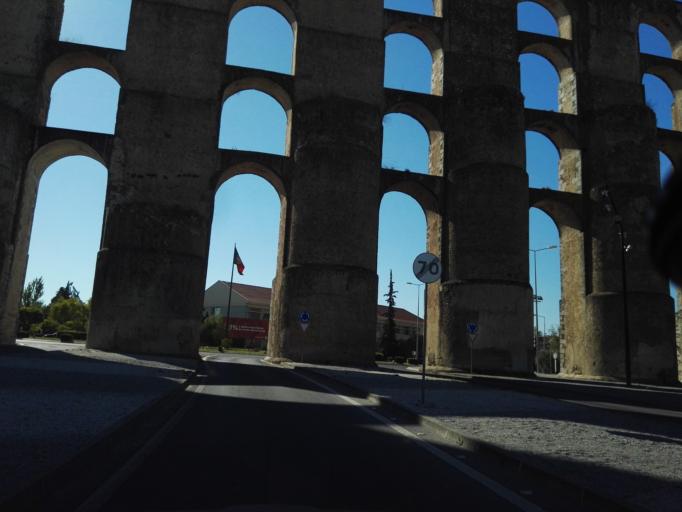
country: PT
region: Portalegre
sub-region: Elvas
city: Elvas
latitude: 38.8783
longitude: -7.1726
